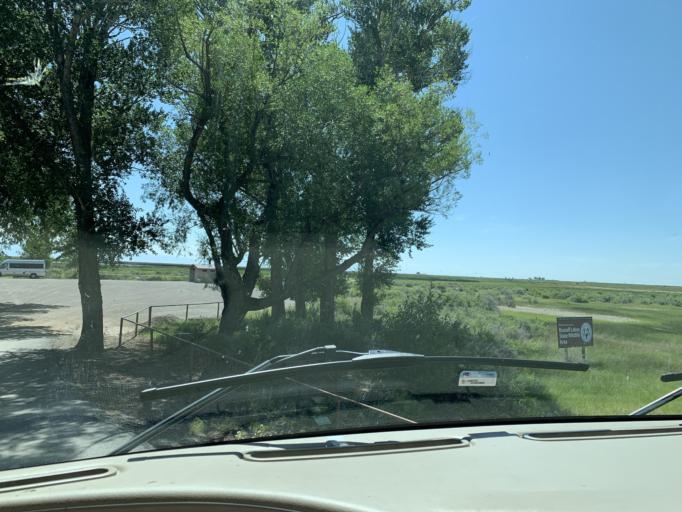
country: US
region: Colorado
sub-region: Saguache County
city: Saguache
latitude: 37.9383
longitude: -106.1447
